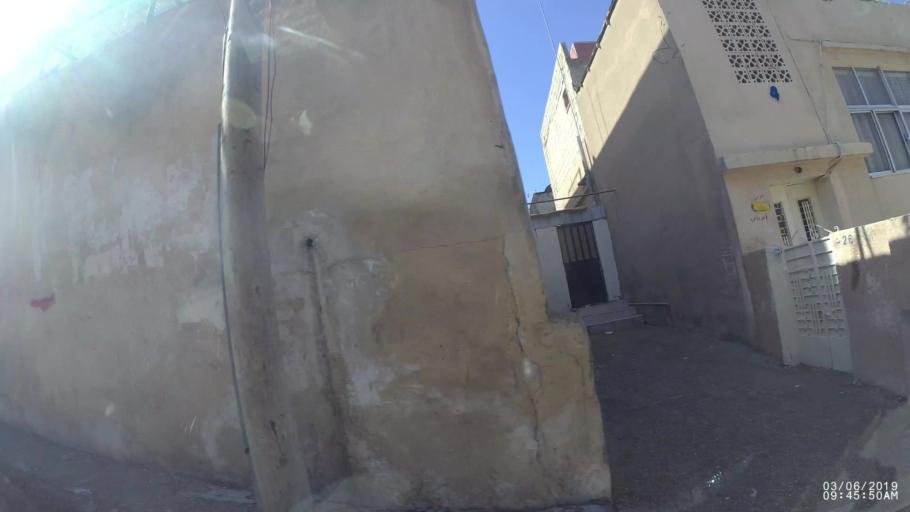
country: JO
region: Amman
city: Amman
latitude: 31.9879
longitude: 35.9863
